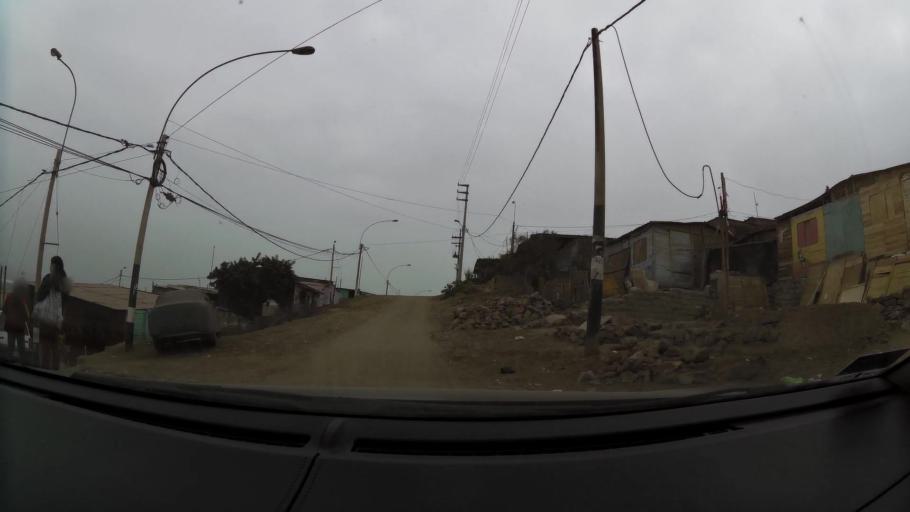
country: PE
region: Lima
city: Ventanilla
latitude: -11.8479
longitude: -77.1560
